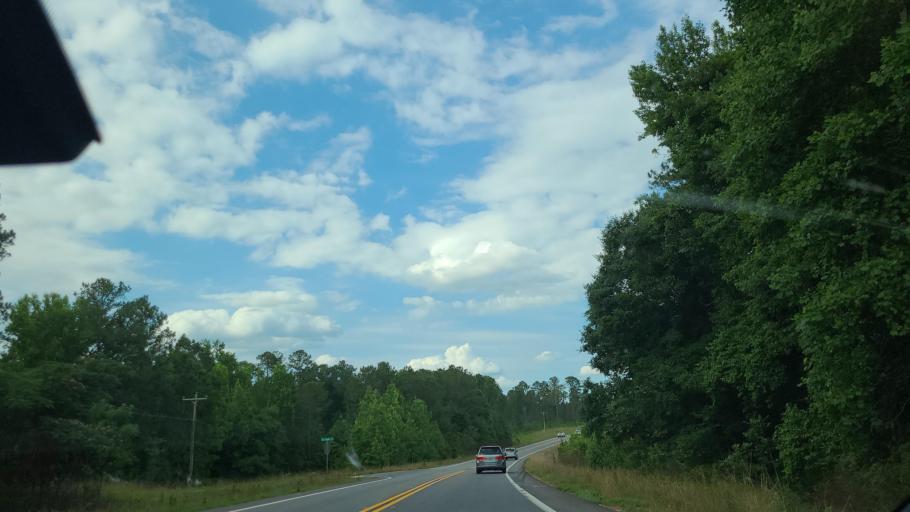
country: US
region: Georgia
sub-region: Putnam County
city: Eatonton
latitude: 33.2542
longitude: -83.4269
